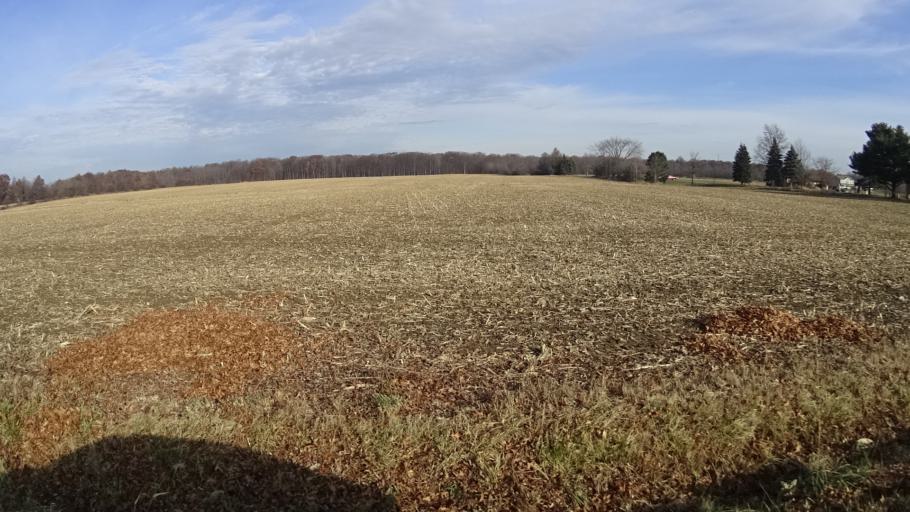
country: US
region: Ohio
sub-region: Lorain County
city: Grafton
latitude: 41.2073
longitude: -81.9747
